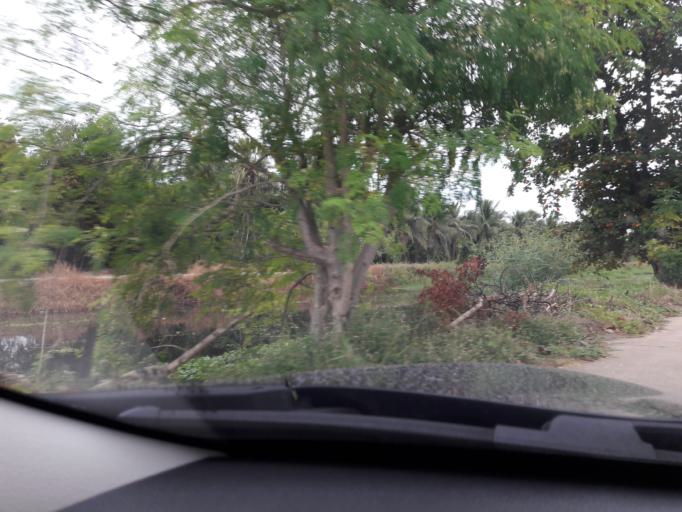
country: TH
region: Ratchaburi
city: Damnoen Saduak
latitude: 13.6054
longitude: 99.9727
